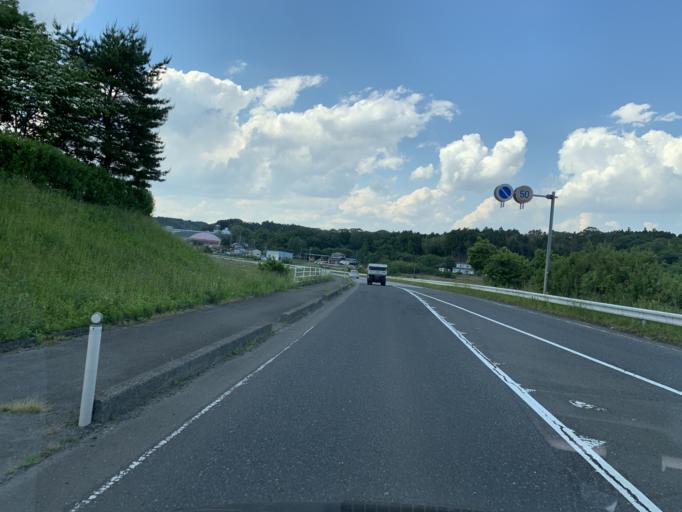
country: JP
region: Miyagi
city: Wakuya
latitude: 38.5407
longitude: 141.1497
